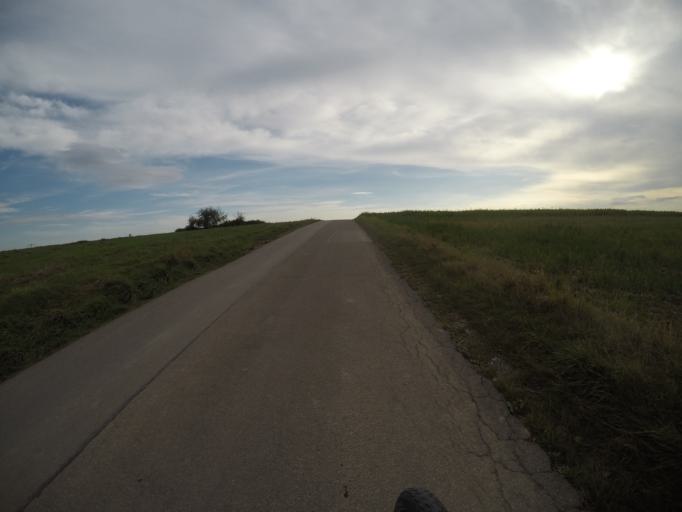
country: DE
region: Baden-Wuerttemberg
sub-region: Regierungsbezirk Stuttgart
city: Herrenberg
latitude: 48.5506
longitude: 8.9221
